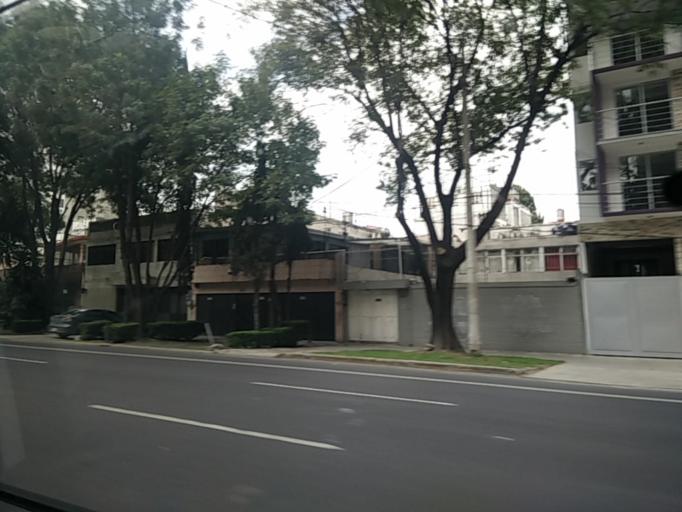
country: MX
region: Mexico City
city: Colonia del Valle
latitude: 19.3755
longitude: -99.1600
